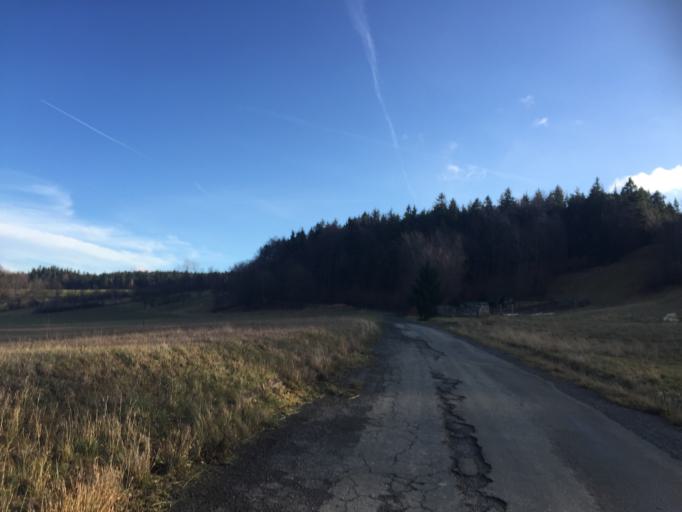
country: DE
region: Thuringia
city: Doschnitz
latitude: 50.6505
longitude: 11.2403
